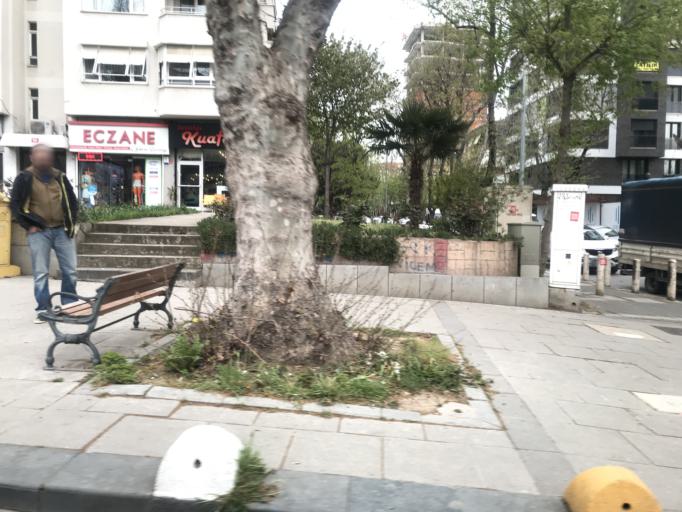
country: TR
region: Istanbul
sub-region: Atasehir
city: Atasehir
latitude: 40.9628
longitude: 29.0906
